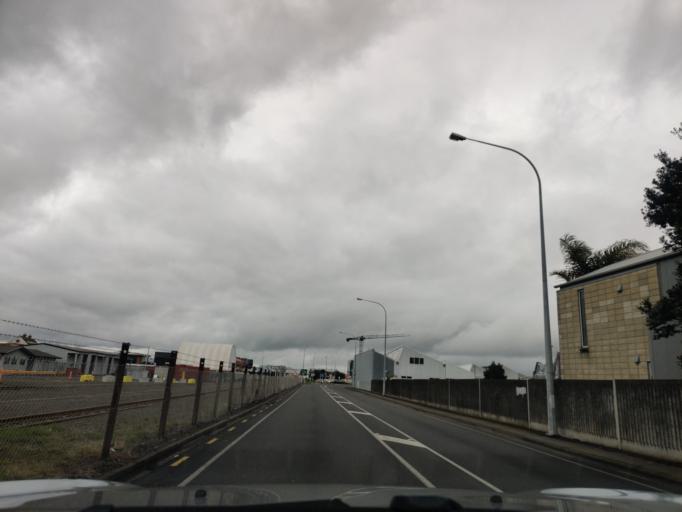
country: NZ
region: Hawke's Bay
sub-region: Napier City
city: Napier
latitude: -39.4809
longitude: 176.8999
